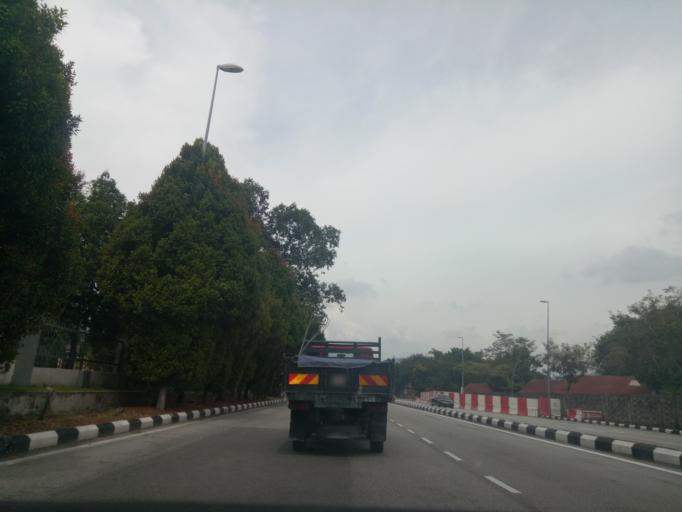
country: MY
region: Perak
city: Ipoh
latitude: 4.5947
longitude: 101.1204
